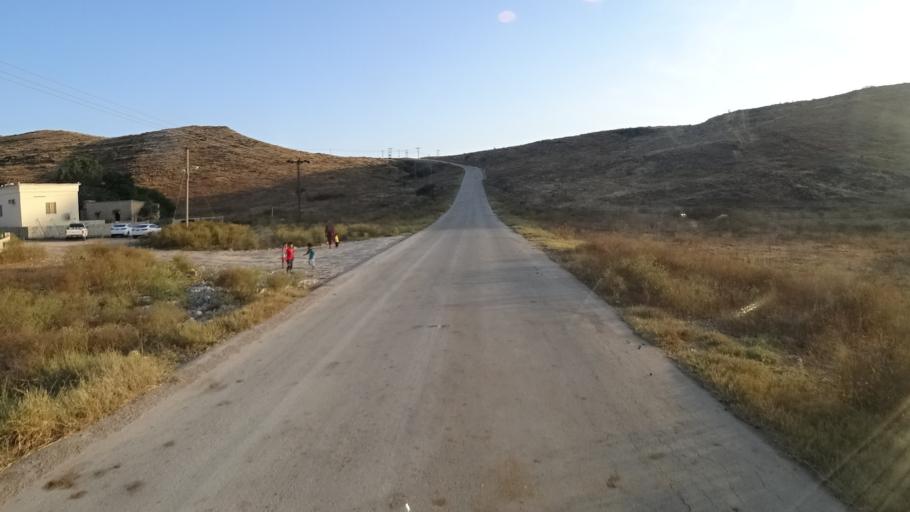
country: OM
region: Zufar
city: Salalah
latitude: 17.1525
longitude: 54.6181
